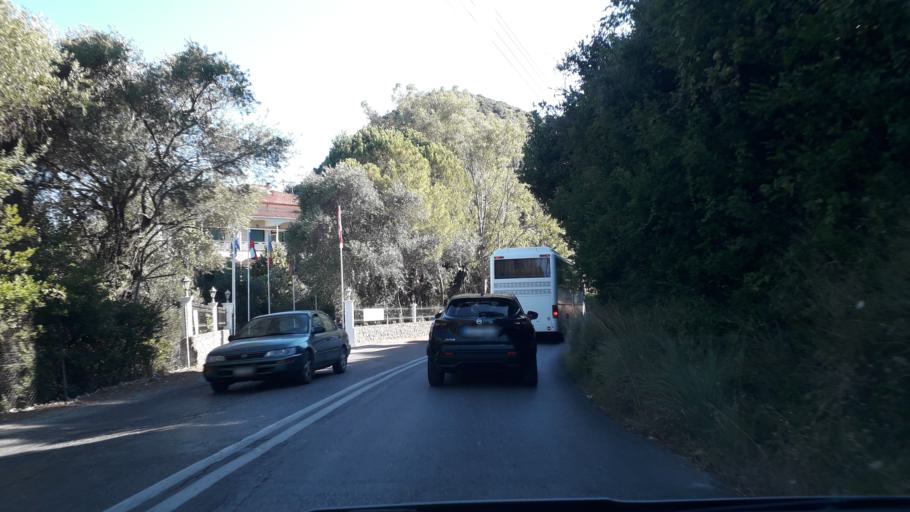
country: GR
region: Ionian Islands
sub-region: Nomos Kerkyras
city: Agios Matthaios
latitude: 39.5132
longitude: 19.9236
